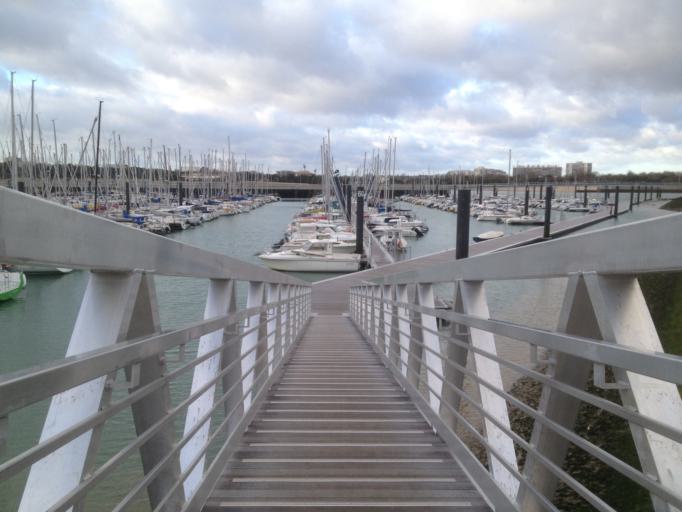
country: FR
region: Poitou-Charentes
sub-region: Departement de la Charente-Maritime
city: La Rochelle
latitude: 46.1488
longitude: -1.1610
